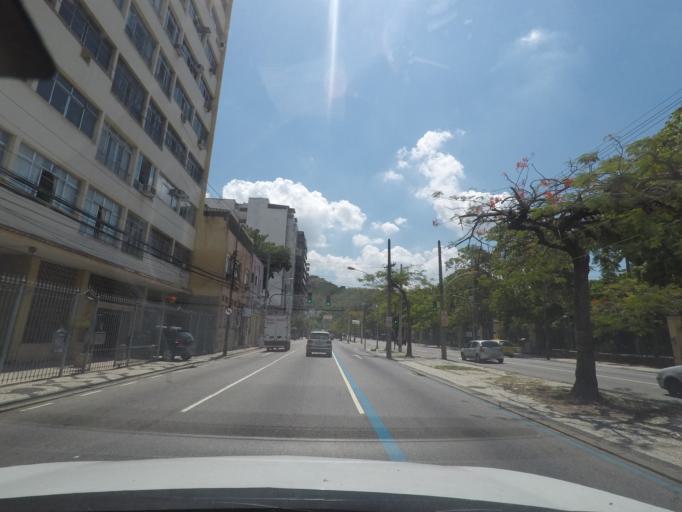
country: BR
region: Rio de Janeiro
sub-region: Rio De Janeiro
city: Rio de Janeiro
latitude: -22.9169
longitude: -43.2593
